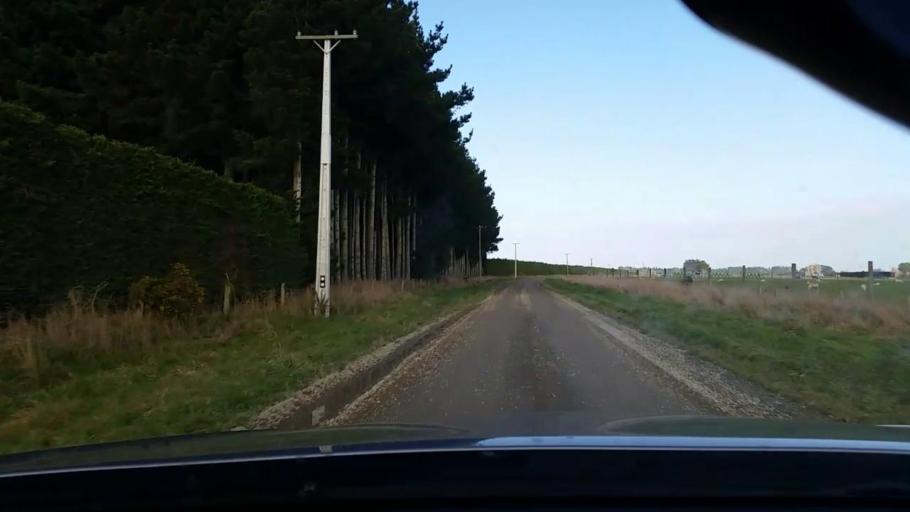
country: NZ
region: Southland
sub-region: Invercargill City
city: Invercargill
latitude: -46.2813
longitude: 168.2942
